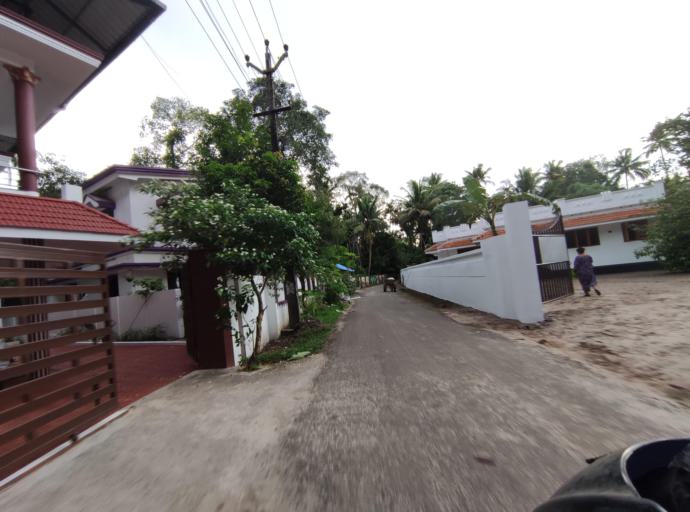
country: IN
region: Kerala
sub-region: Alappuzha
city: Shertallai
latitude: 9.6705
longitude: 76.3469
